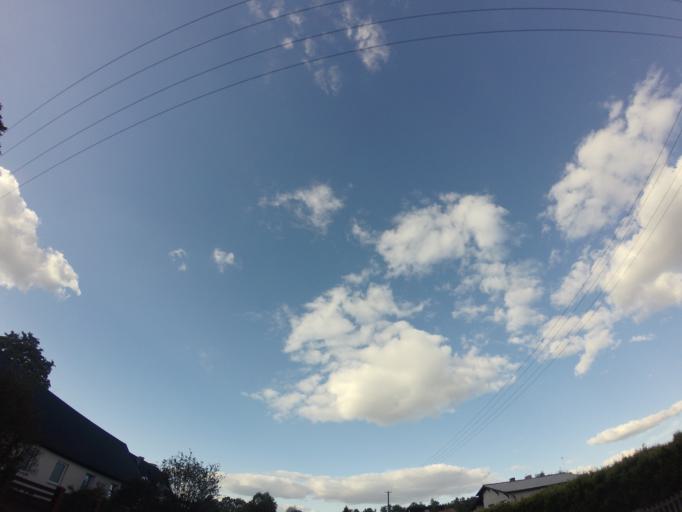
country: PL
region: Greater Poland Voivodeship
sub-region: Powiat nowotomyski
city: Nowy Tomysl
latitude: 52.2728
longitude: 16.1273
